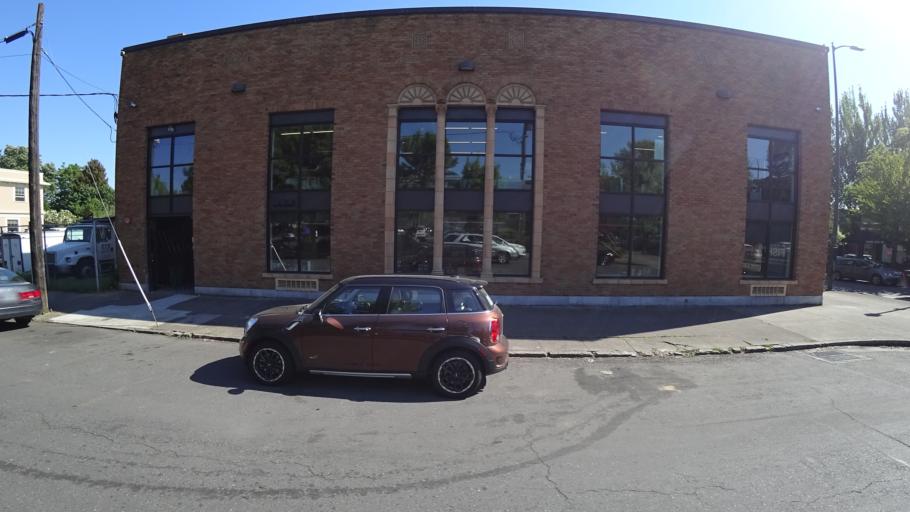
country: US
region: Oregon
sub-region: Multnomah County
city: Portland
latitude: 45.5413
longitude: -122.6612
